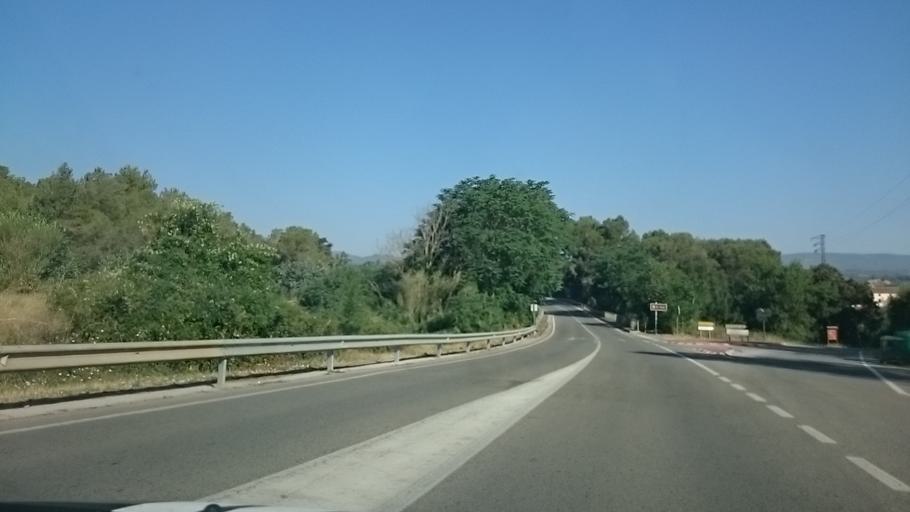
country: ES
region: Catalonia
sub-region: Provincia de Barcelona
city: Vilobi del Penedes
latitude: 41.3830
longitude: 1.6350
